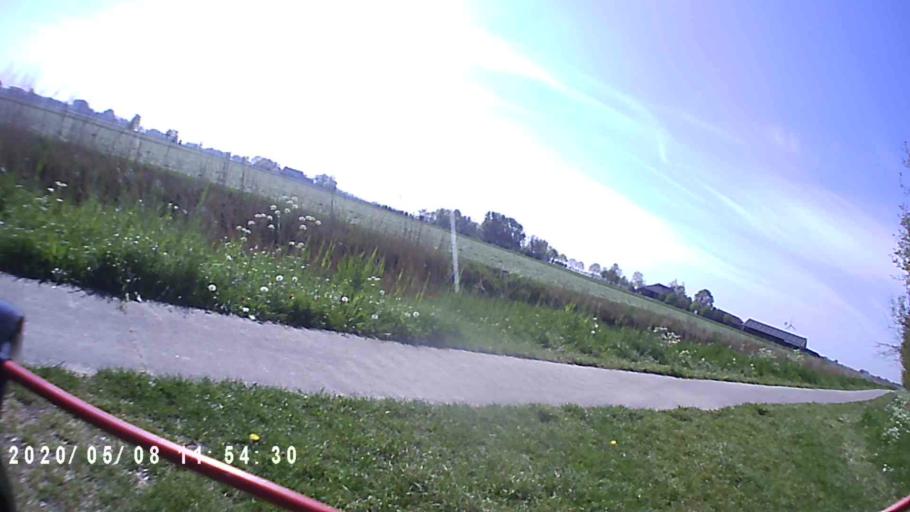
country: NL
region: Groningen
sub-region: Gemeente Bedum
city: Bedum
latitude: 53.3173
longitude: 6.6915
